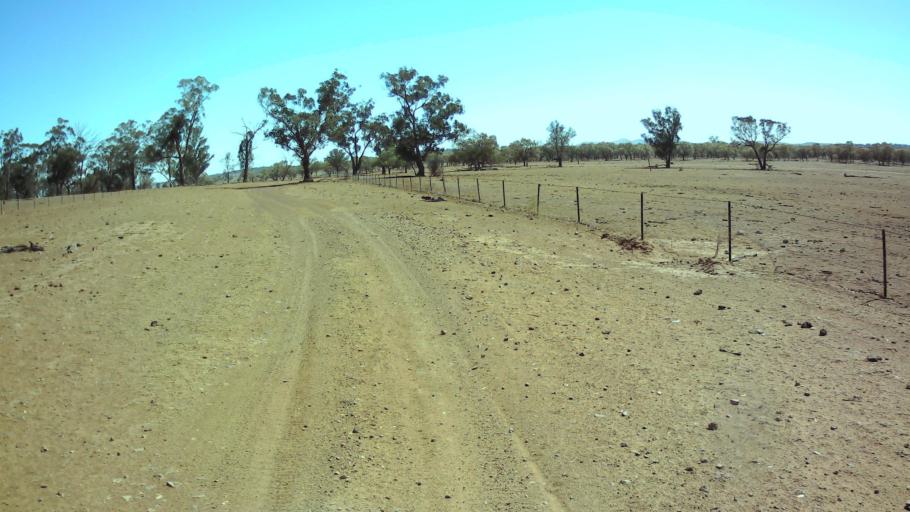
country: AU
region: New South Wales
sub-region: Forbes
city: Forbes
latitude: -33.7313
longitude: 147.6656
